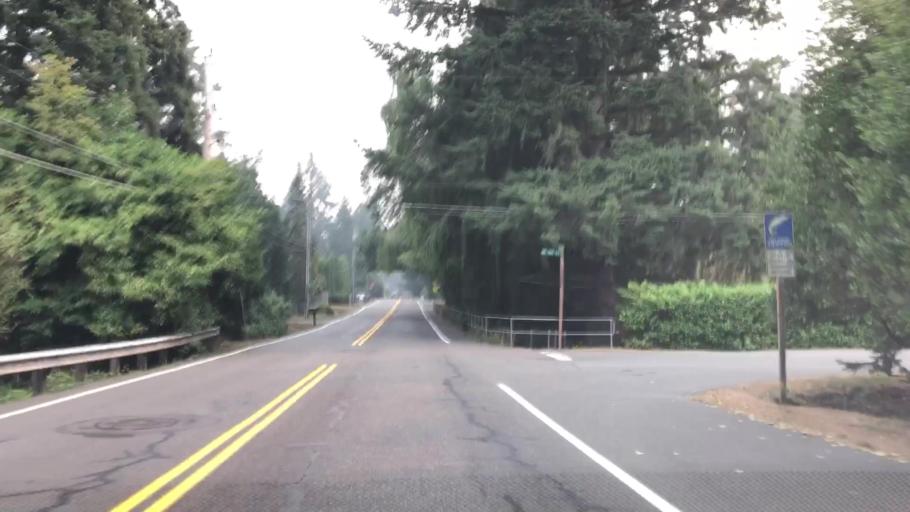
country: US
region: Washington
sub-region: King County
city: Lake Forest Park
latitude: 47.7666
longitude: -122.2919
